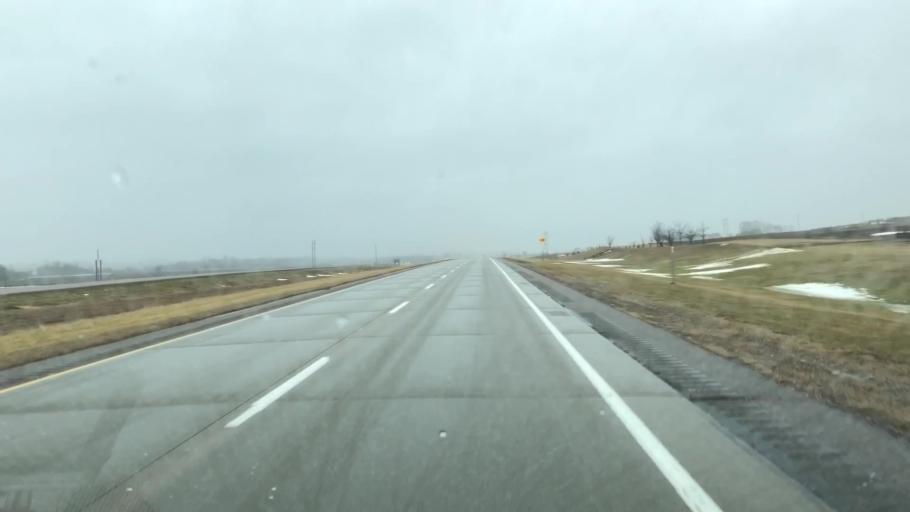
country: US
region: Iowa
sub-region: Sioux County
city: Orange City
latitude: 42.8994
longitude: -96.0871
